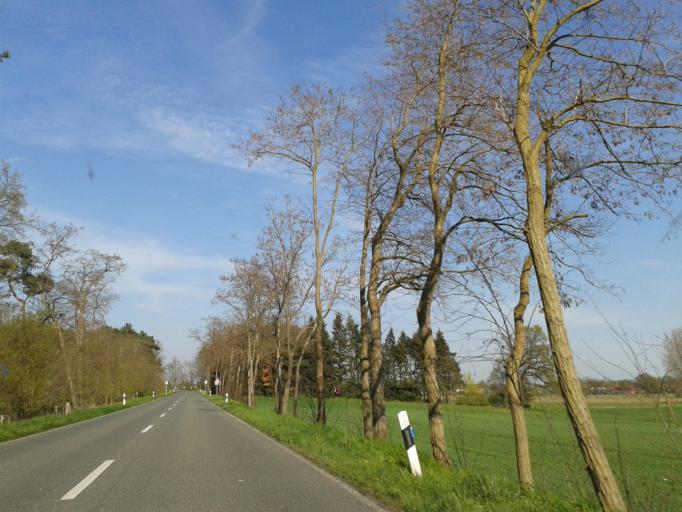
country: DE
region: North Rhine-Westphalia
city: Geseke
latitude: 51.7077
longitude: 8.5102
